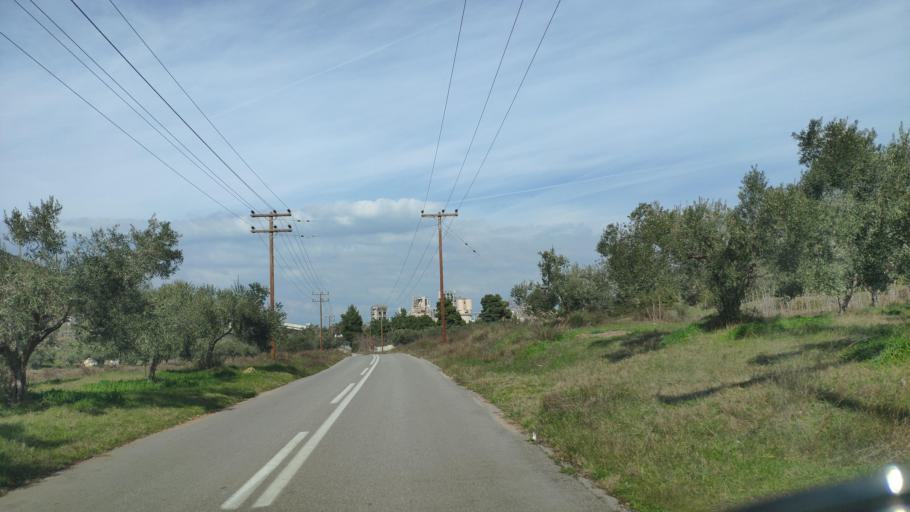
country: GR
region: Central Greece
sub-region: Nomos Evvoias
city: Vathi
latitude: 38.4304
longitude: 23.5922
